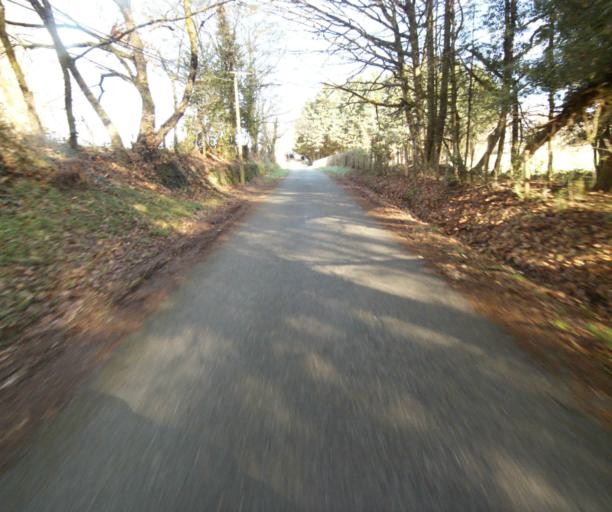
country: FR
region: Limousin
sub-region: Departement de la Correze
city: Laguenne
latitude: 45.2809
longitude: 1.8560
